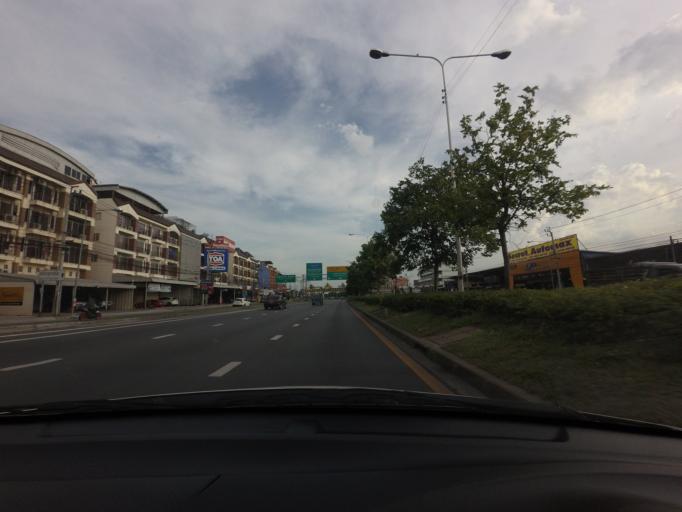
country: TH
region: Nonthaburi
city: Bang Kruai
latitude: 13.8419
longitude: 100.4479
